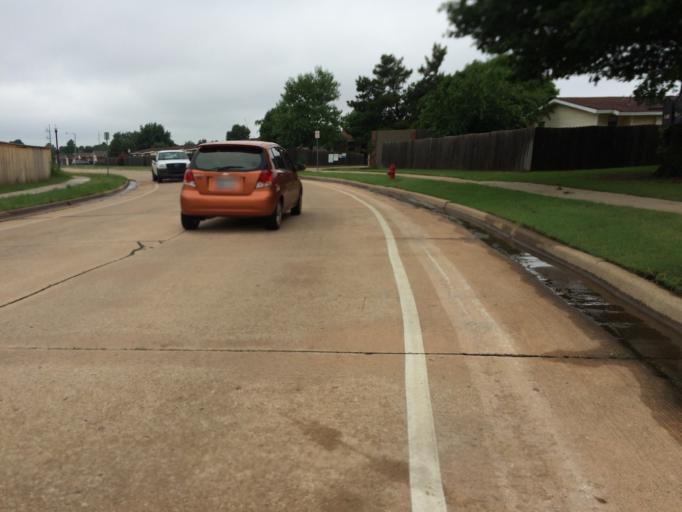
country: US
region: Oklahoma
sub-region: Cleveland County
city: Hall Park
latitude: 35.2076
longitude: -97.4094
